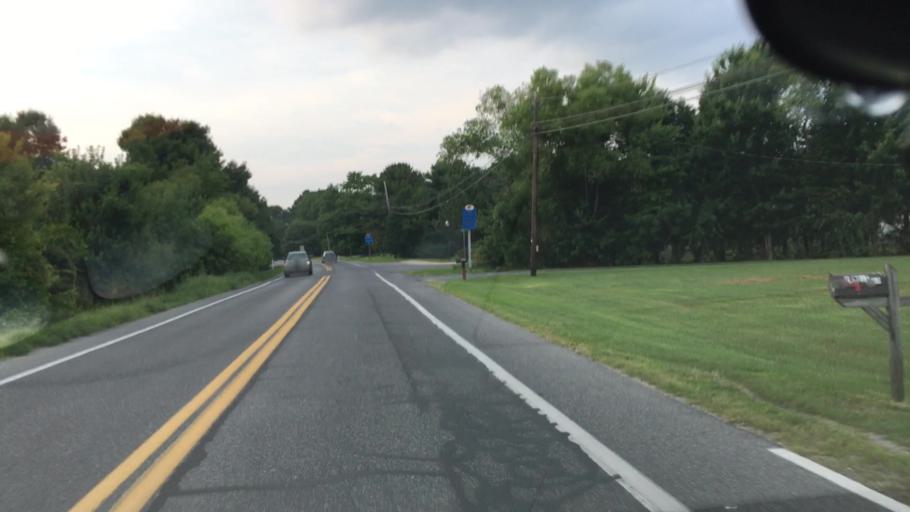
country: US
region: Delaware
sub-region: Sussex County
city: Ocean View
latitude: 38.5343
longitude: -75.0892
